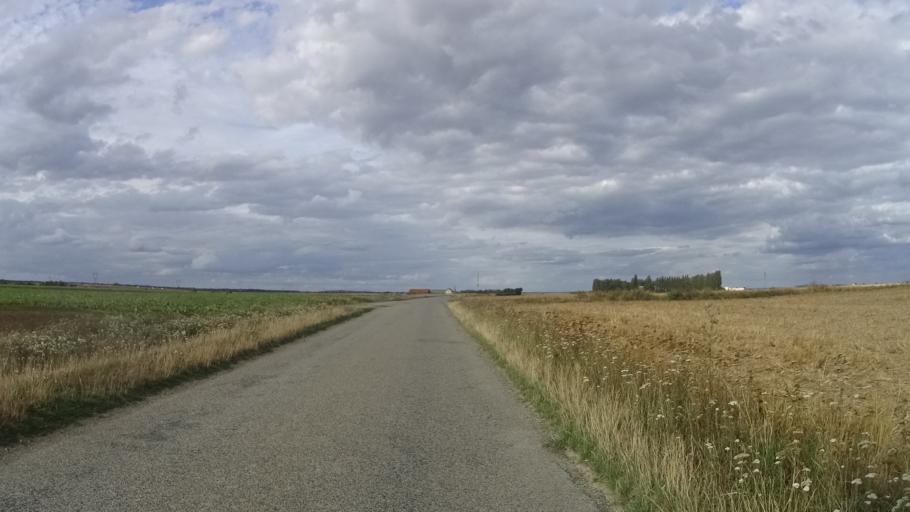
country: FR
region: Picardie
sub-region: Departement de l'Oise
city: Lagny-le-Sec
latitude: 49.1051
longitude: 2.7196
